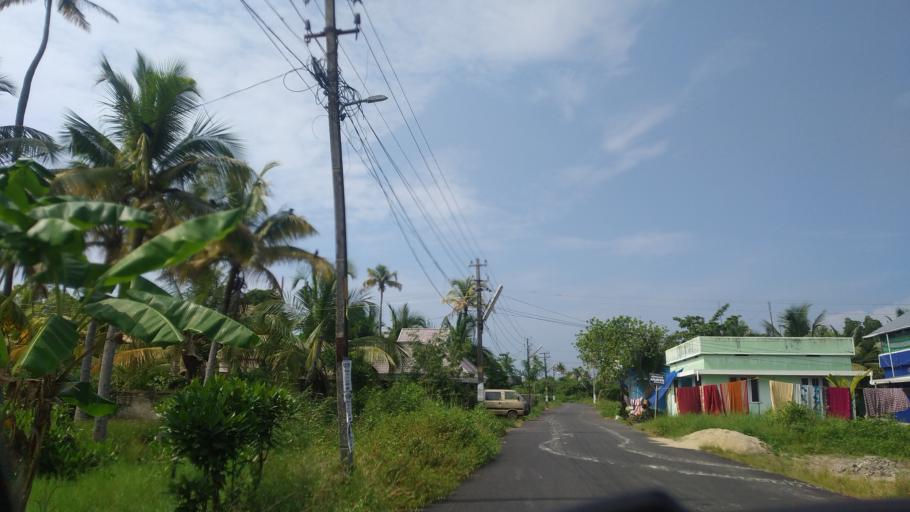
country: IN
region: Kerala
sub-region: Ernakulam
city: Elur
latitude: 10.0464
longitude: 76.2073
